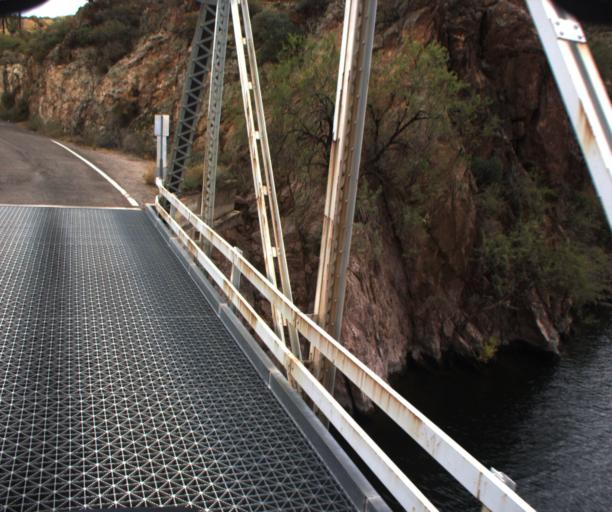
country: US
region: Arizona
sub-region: Pinal County
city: Apache Junction
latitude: 33.5389
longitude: -111.4434
